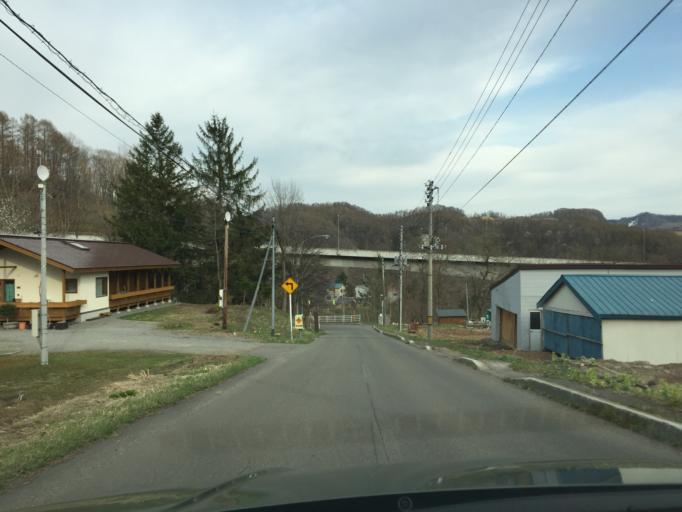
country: JP
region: Hokkaido
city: Utashinai
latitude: 43.5205
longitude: 142.0227
